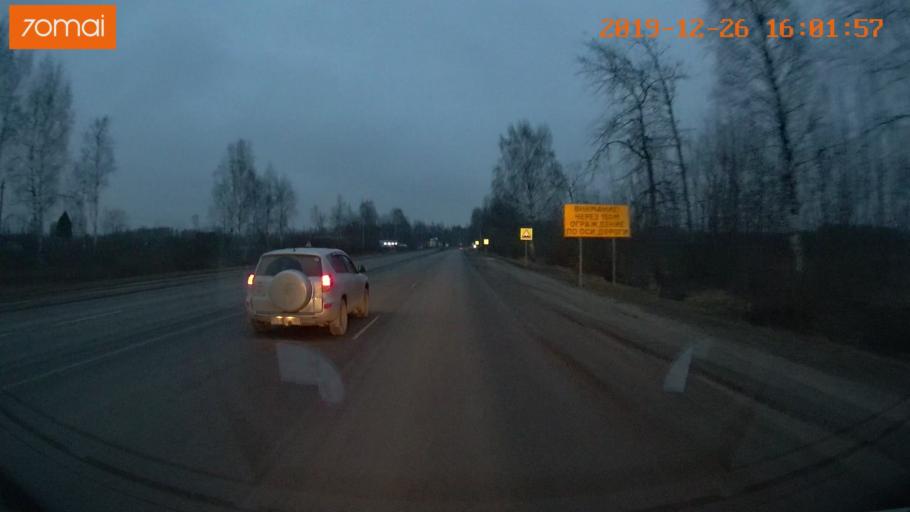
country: RU
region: Jaroslavl
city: Rybinsk
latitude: 58.0148
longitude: 38.8250
